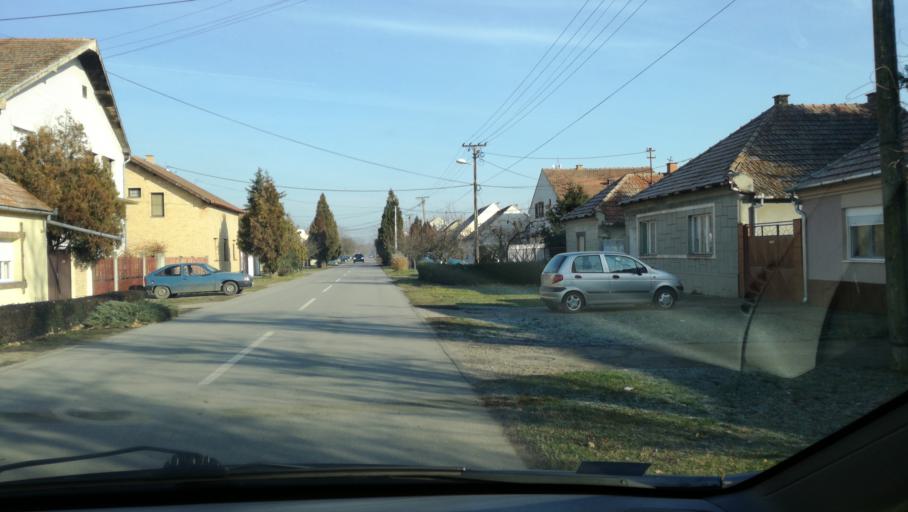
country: RS
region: Autonomna Pokrajina Vojvodina
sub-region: Severnobanatski Okrug
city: Kikinda
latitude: 45.8217
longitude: 20.4497
